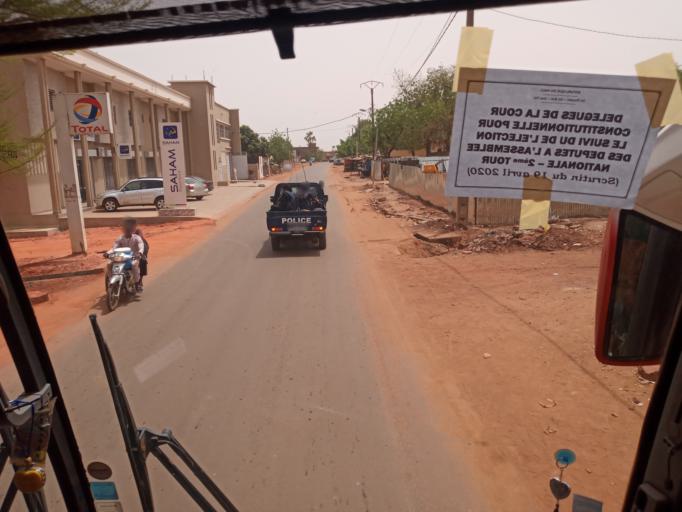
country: ML
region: Koulikoro
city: Koulikoro
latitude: 12.8578
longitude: -7.5609
